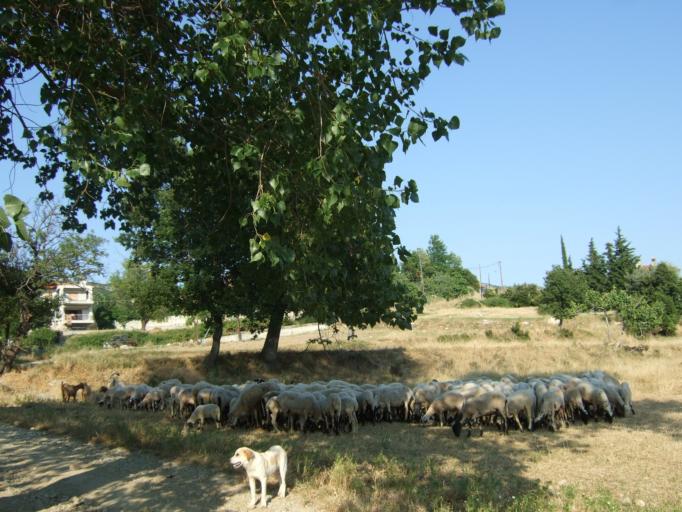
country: GR
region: Central Macedonia
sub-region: Nomos Thessalonikis
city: Peristera
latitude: 40.5489
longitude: 23.1588
